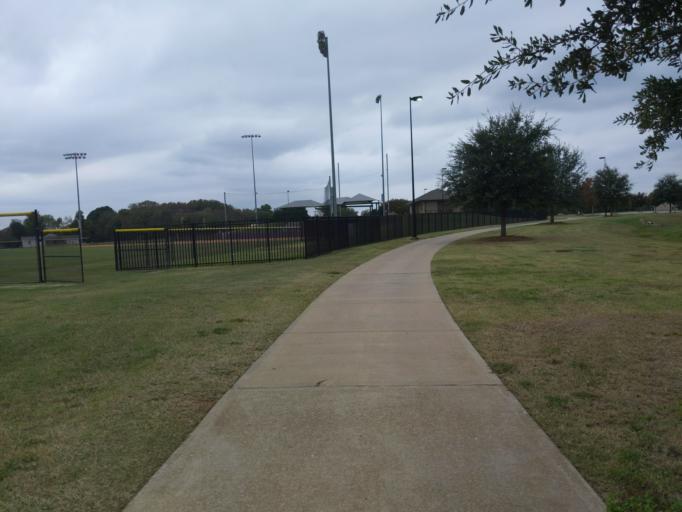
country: US
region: South Carolina
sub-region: Spartanburg County
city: Duncan
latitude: 34.8710
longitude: -82.1052
